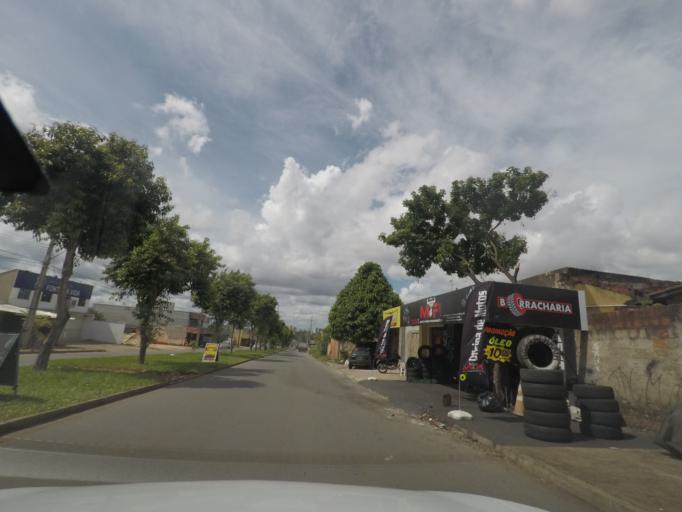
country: BR
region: Goias
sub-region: Goiania
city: Goiania
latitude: -16.7262
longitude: -49.3388
